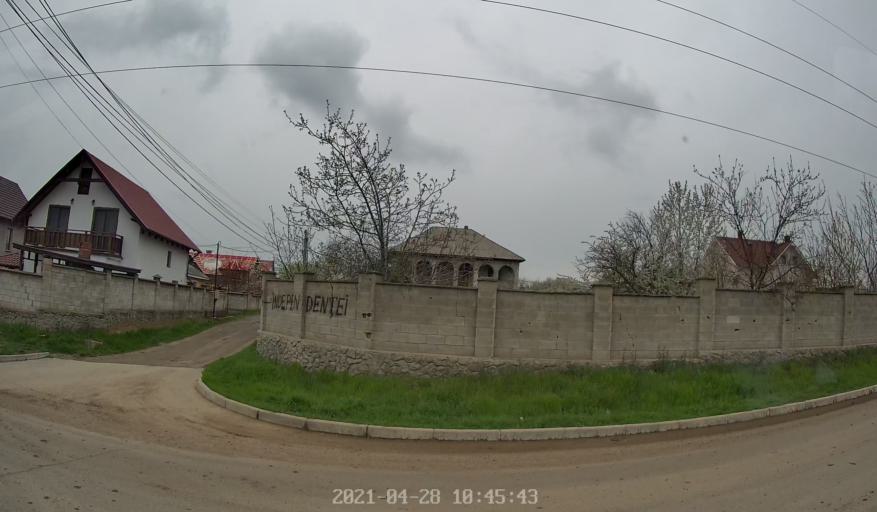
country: MD
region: Chisinau
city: Singera
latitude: 46.9888
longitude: 28.9411
